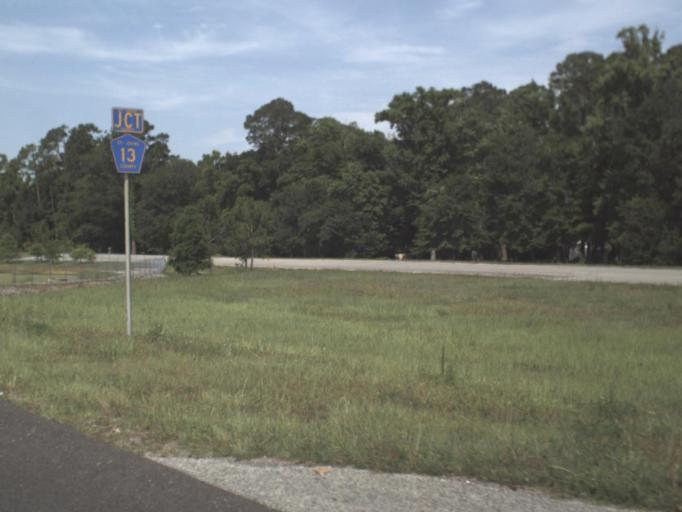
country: US
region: Florida
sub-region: Putnam County
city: East Palatka
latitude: 29.7438
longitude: -81.4728
